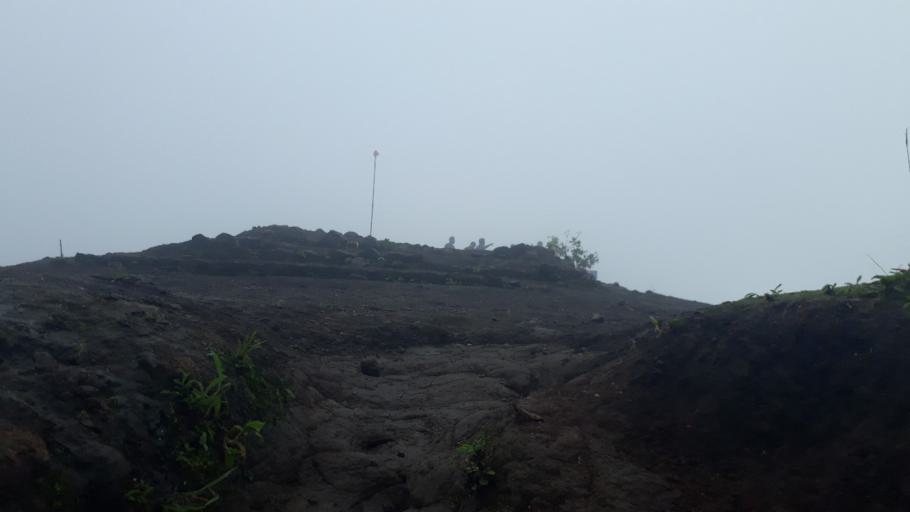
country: IN
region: Maharashtra
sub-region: Pune Division
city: Lonavla
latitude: 18.6318
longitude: 73.5127
